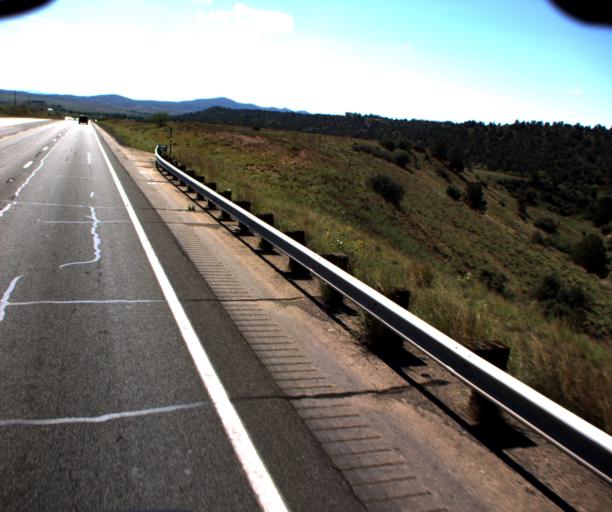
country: US
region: Arizona
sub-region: Yavapai County
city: Prescott Valley
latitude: 34.5765
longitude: -112.2890
